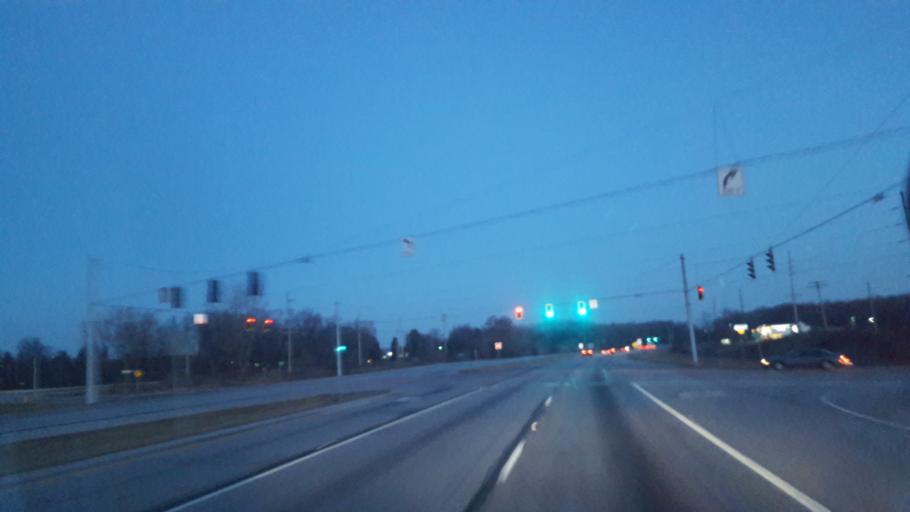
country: US
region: Indiana
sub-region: Kosciusko County
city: Warsaw
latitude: 41.2639
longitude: -85.8431
